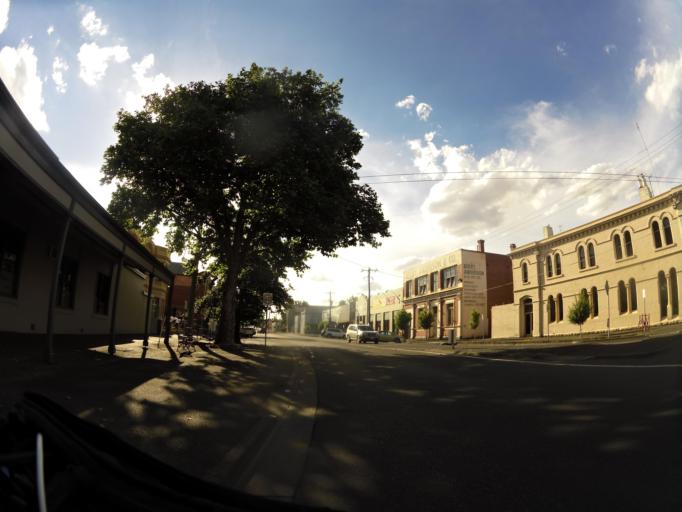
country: AU
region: Victoria
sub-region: Ballarat North
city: Ballarat Central
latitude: -37.5643
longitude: 143.8572
